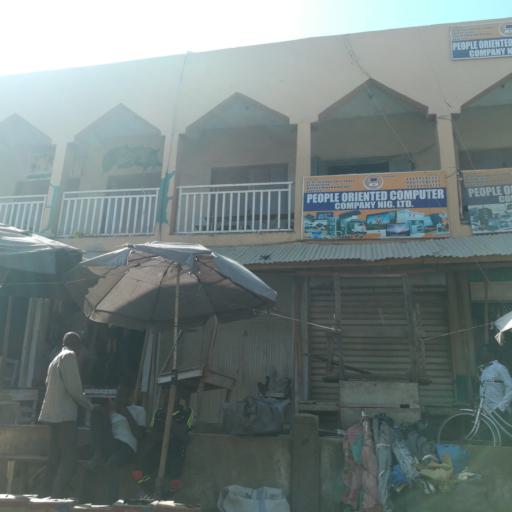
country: NG
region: Kano
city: Kano
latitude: 12.0101
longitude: 8.5385
